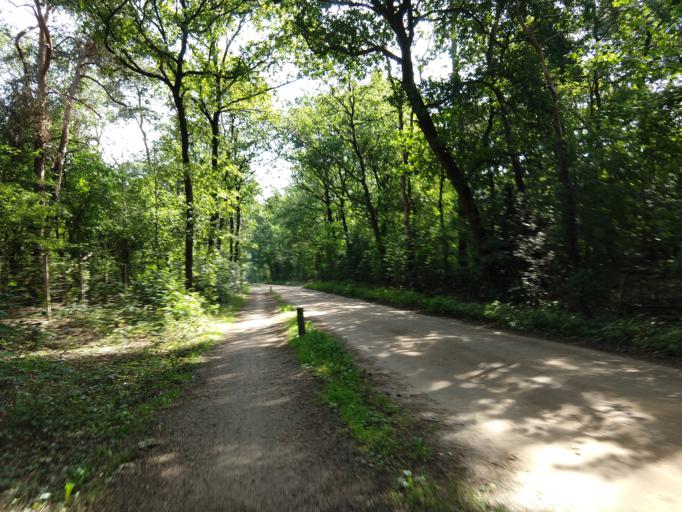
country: NL
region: Gelderland
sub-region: Gemeente Ede
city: Otterlo
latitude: 52.1084
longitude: 5.7698
